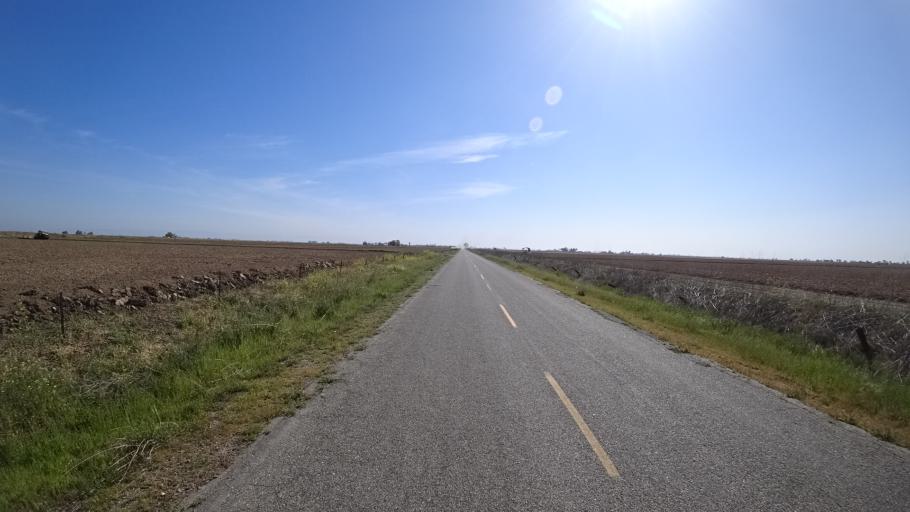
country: US
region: California
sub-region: Glenn County
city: Willows
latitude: 39.5389
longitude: -122.1619
